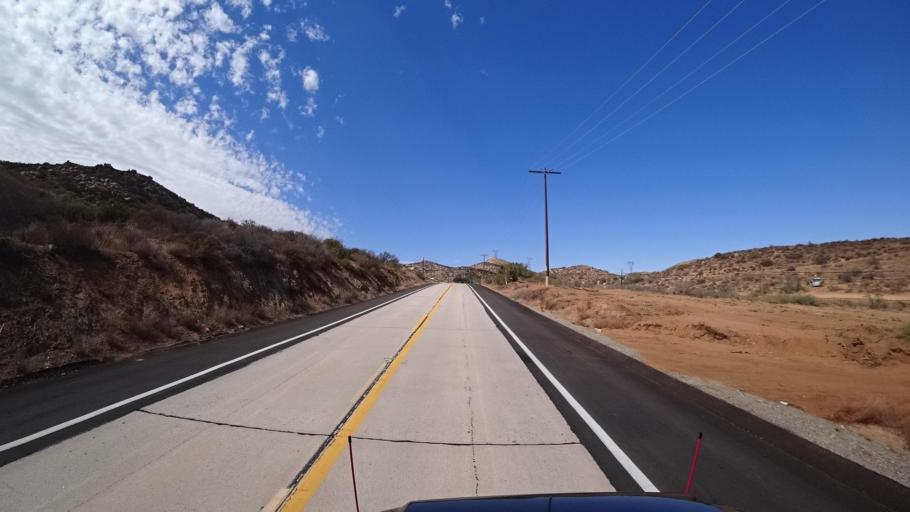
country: MX
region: Baja California
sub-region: Tecate
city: Cereso del Hongo
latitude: 32.6375
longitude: -116.2274
